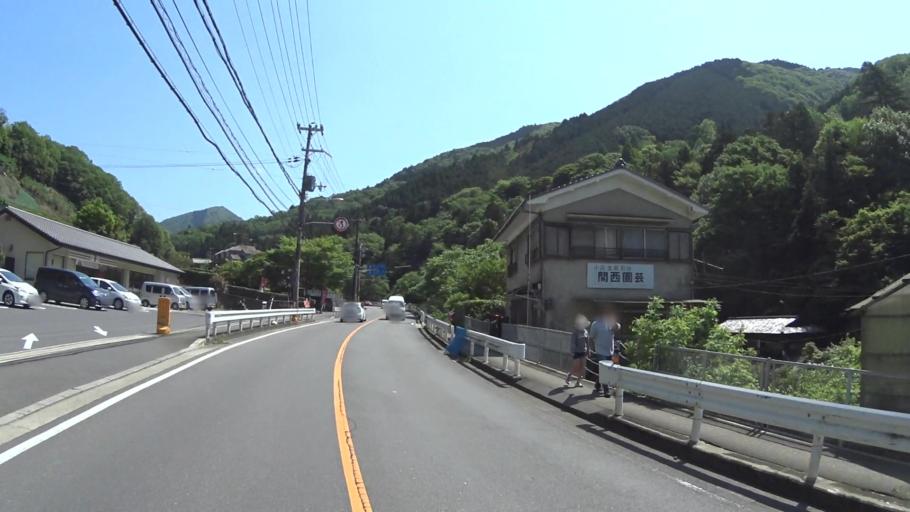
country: JP
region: Kyoto
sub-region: Kyoto-shi
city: Kamigyo-ku
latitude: 35.0676
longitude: 135.8086
